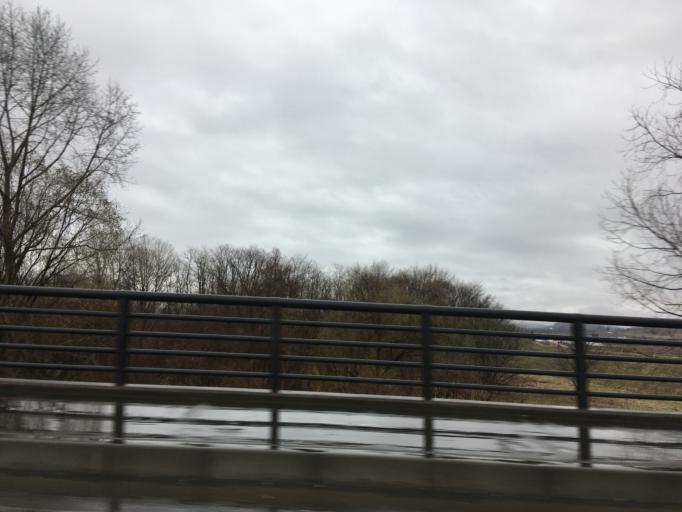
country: JP
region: Hokkaido
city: Nayoro
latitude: 44.1272
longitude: 142.4842
